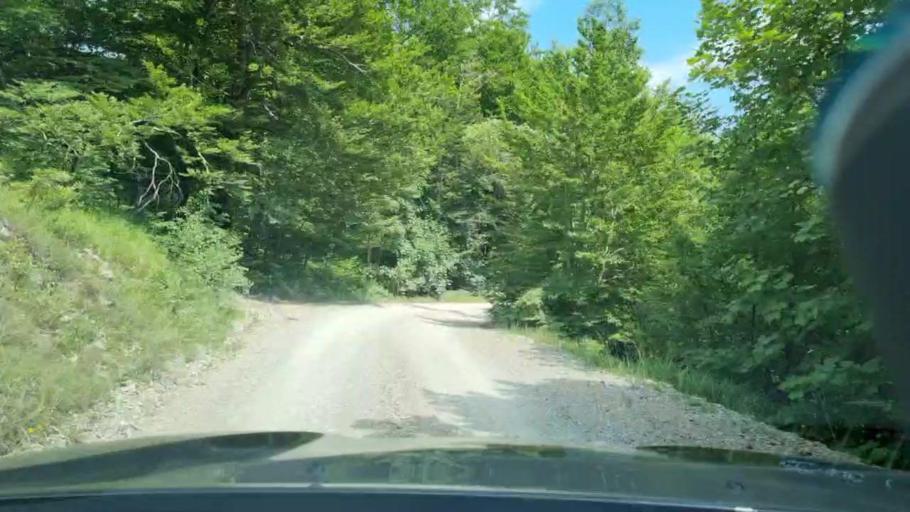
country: BA
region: Federation of Bosnia and Herzegovina
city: Bosansko Grahovo
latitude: 44.2985
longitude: 16.2695
